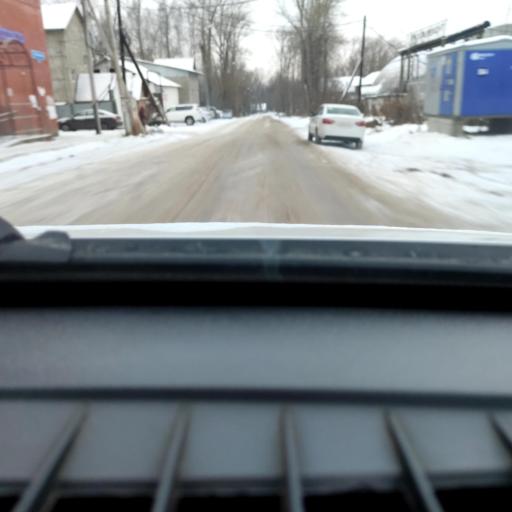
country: RU
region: Perm
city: Perm
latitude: 58.0968
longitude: 56.3704
